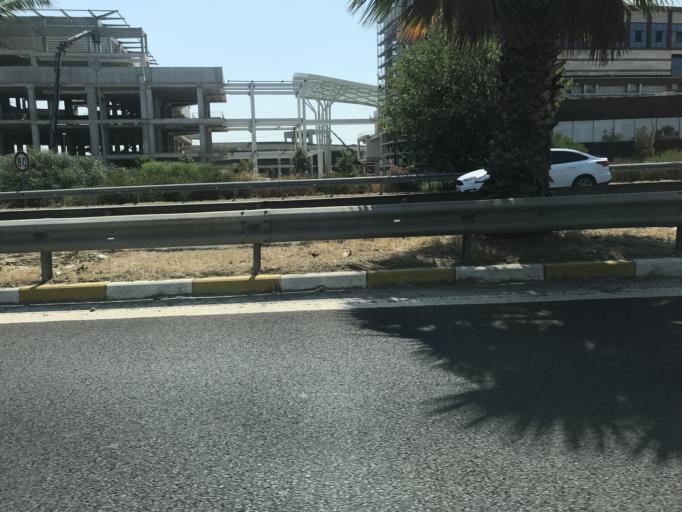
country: TR
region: Izmir
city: Karsiyaka
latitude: 38.4009
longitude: 27.0672
